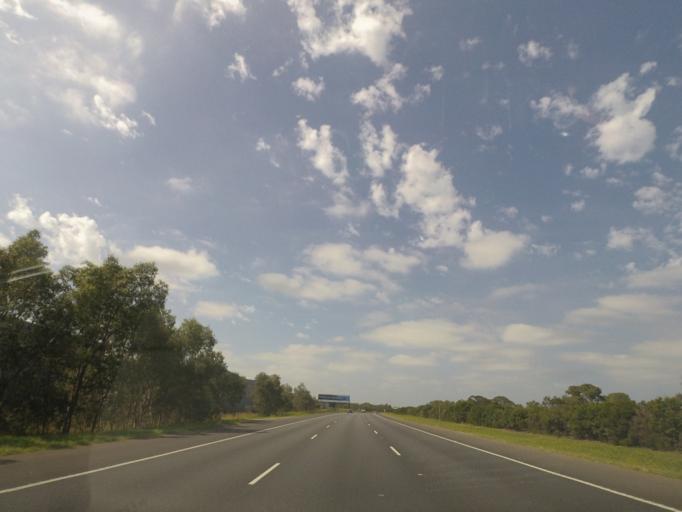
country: AU
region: Victoria
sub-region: Greater Dandenong
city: Keysborough
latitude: -38.0300
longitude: 145.1901
